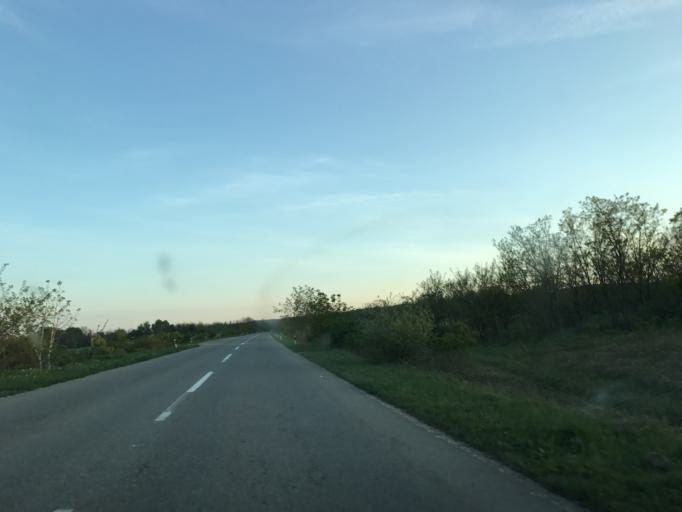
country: RO
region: Mehedinti
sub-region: Comuna Gogosu
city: Ostrovu Mare
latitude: 44.3596
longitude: 22.4786
